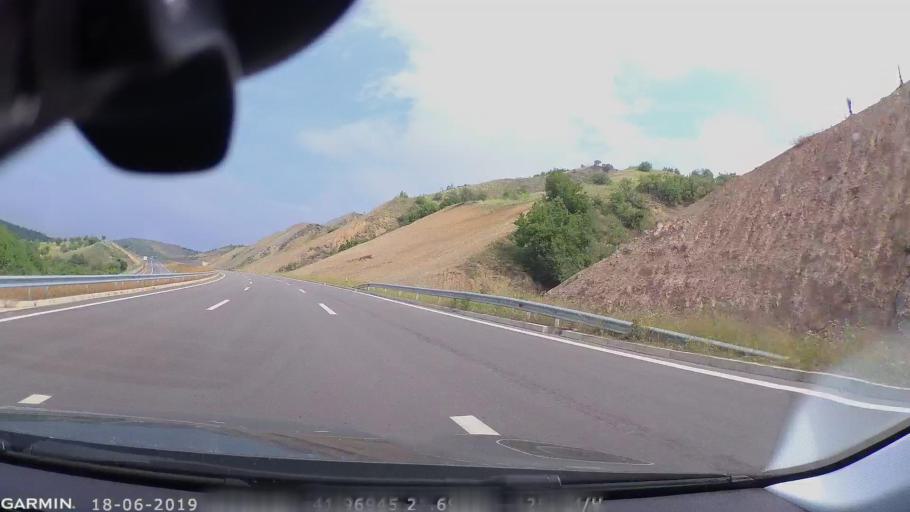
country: MK
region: Petrovec
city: Sredno Konjare
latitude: 41.9456
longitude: 21.7924
